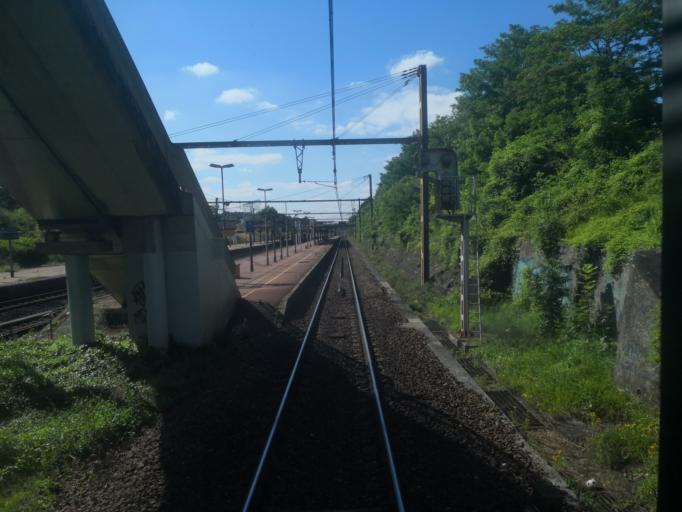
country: FR
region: Ile-de-France
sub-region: Departement de Seine-et-Marne
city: Le Mee-sur-Seine
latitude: 48.5378
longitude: 2.6276
